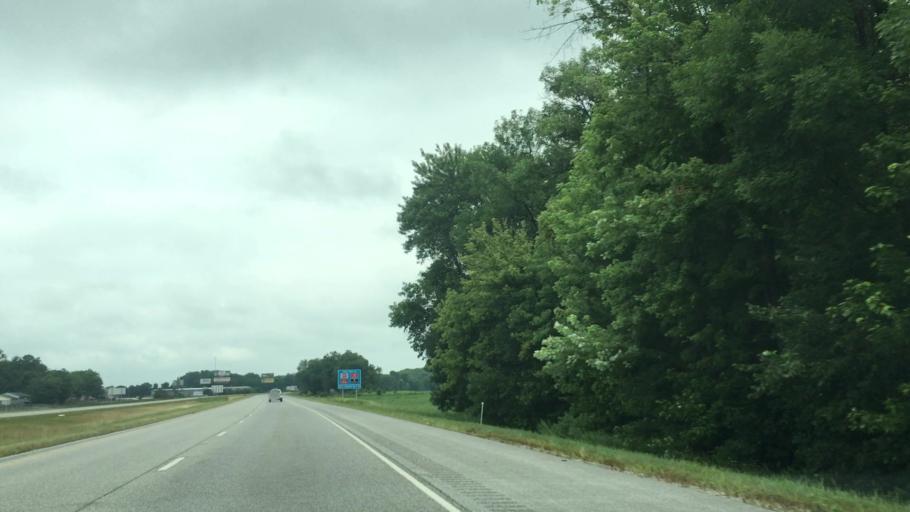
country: US
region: Illinois
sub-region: Rock Island County
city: Moline
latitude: 41.4577
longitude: -90.5159
